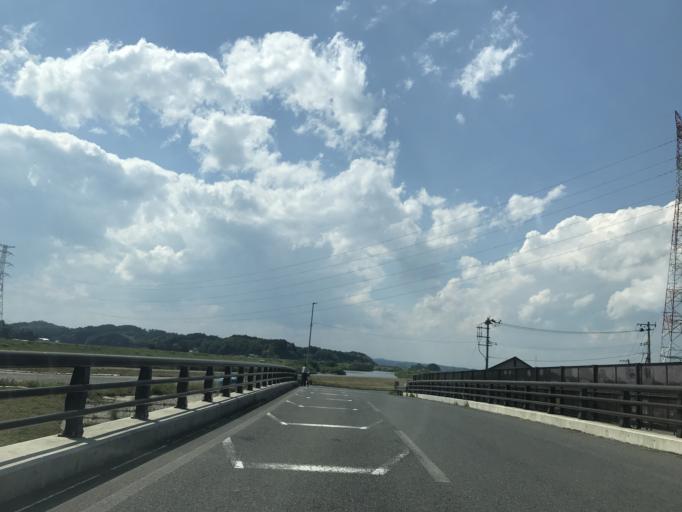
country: JP
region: Miyagi
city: Matsushima
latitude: 38.4293
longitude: 141.1252
